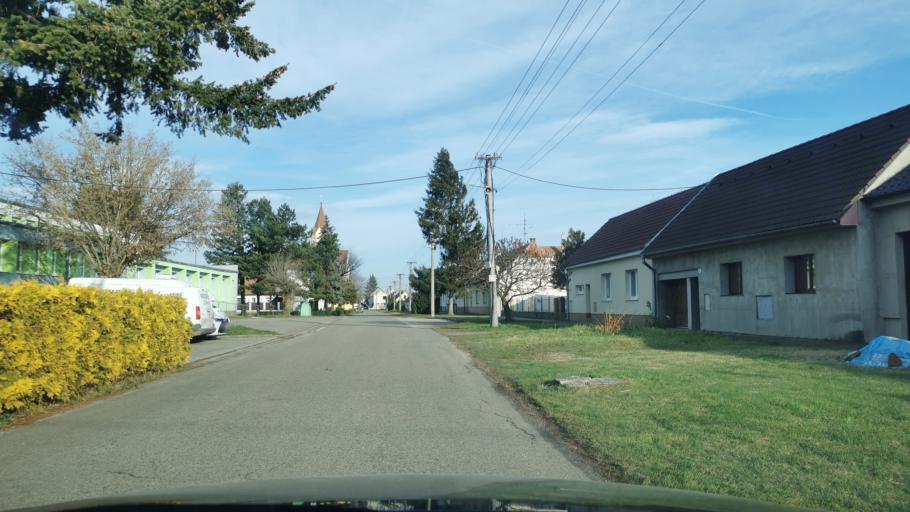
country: SK
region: Trnavsky
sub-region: Okres Skalica
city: Holic
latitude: 48.7872
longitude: 17.1123
